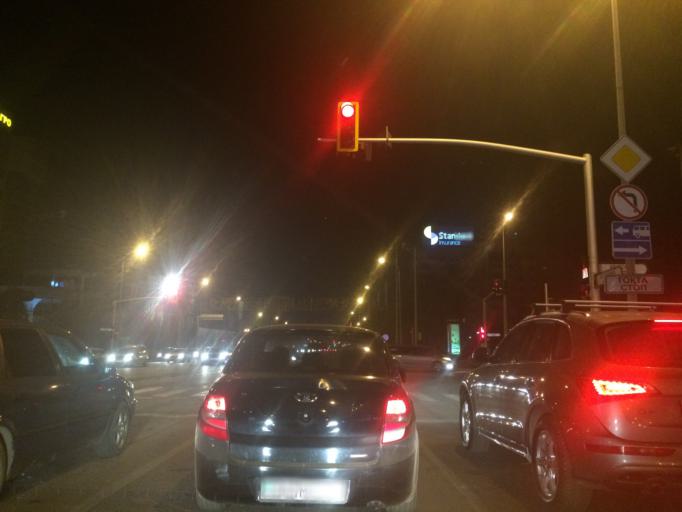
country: KZ
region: Astana Qalasy
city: Astana
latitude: 51.1659
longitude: 71.4271
